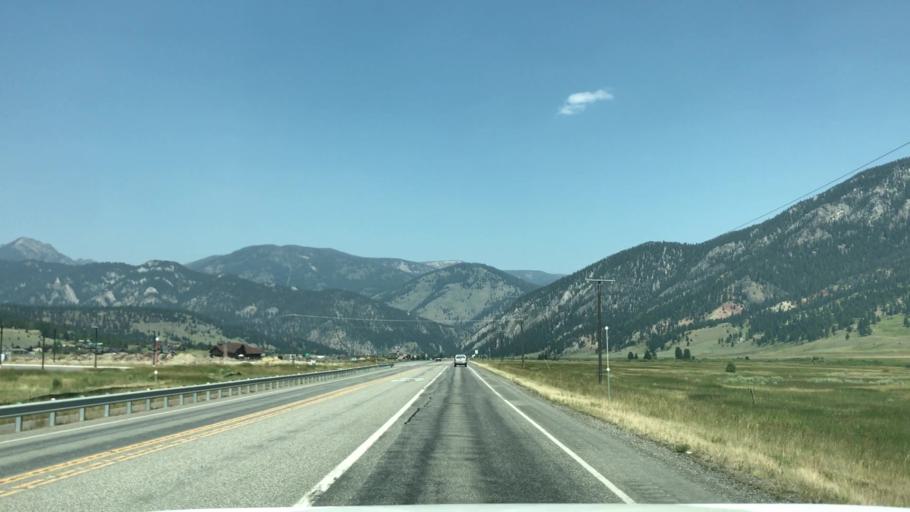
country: US
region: Montana
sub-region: Gallatin County
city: Big Sky
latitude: 45.2304
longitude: -111.2508
